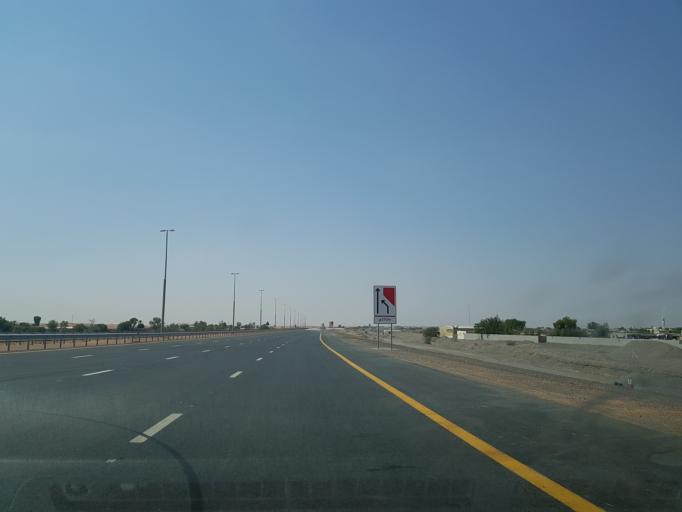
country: AE
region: Ash Shariqah
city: Adh Dhayd
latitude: 25.2329
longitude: 55.9119
